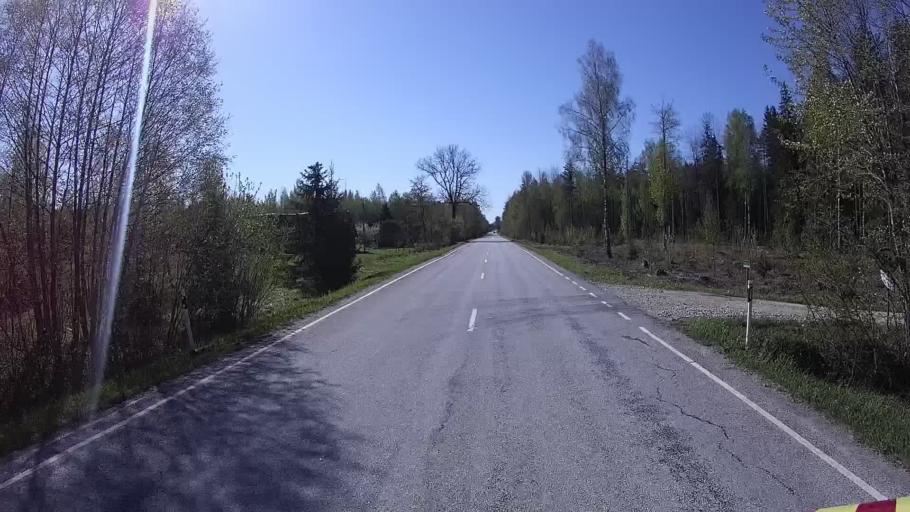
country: EE
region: Raplamaa
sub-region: Jaervakandi vald
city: Jarvakandi
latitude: 58.8015
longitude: 24.8133
